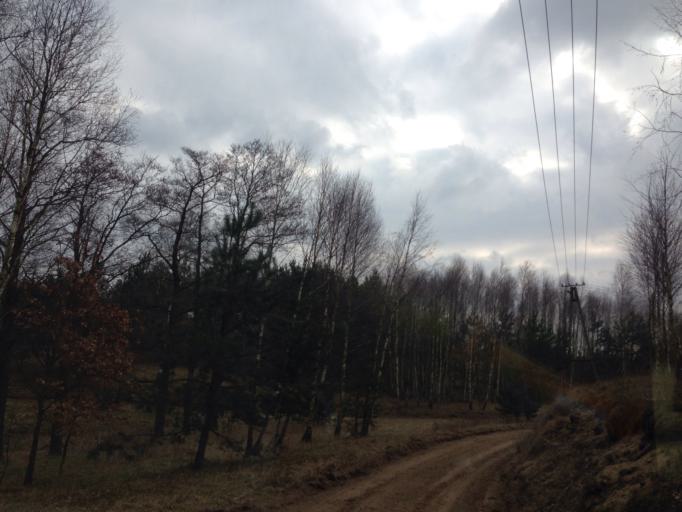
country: PL
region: Warmian-Masurian Voivodeship
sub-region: Powiat dzialdowski
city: Lidzbark
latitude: 53.3726
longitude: 19.7613
